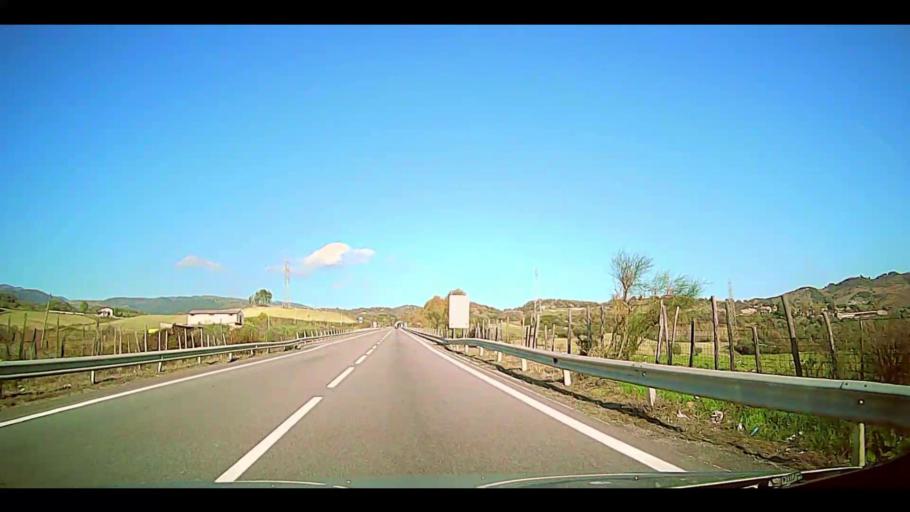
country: IT
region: Calabria
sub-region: Provincia di Crotone
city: Cotronei
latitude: 39.1887
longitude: 16.8167
